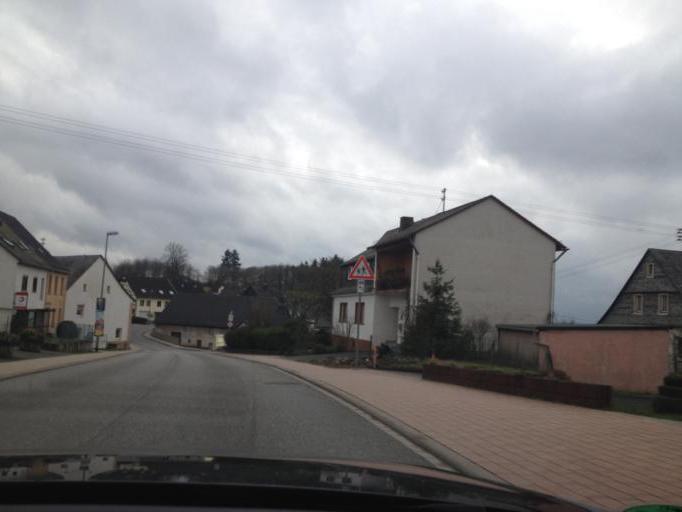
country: DE
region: Rheinland-Pfalz
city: Oberbrombach
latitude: 49.6992
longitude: 7.2612
